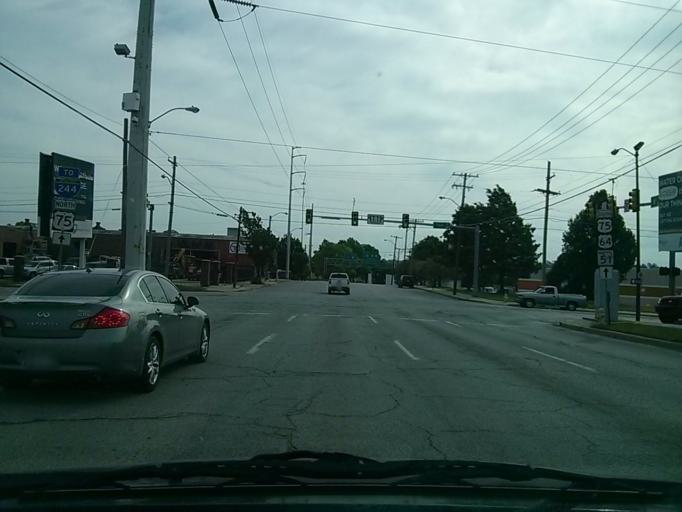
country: US
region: Oklahoma
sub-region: Tulsa County
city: Tulsa
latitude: 36.1501
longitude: -95.9843
